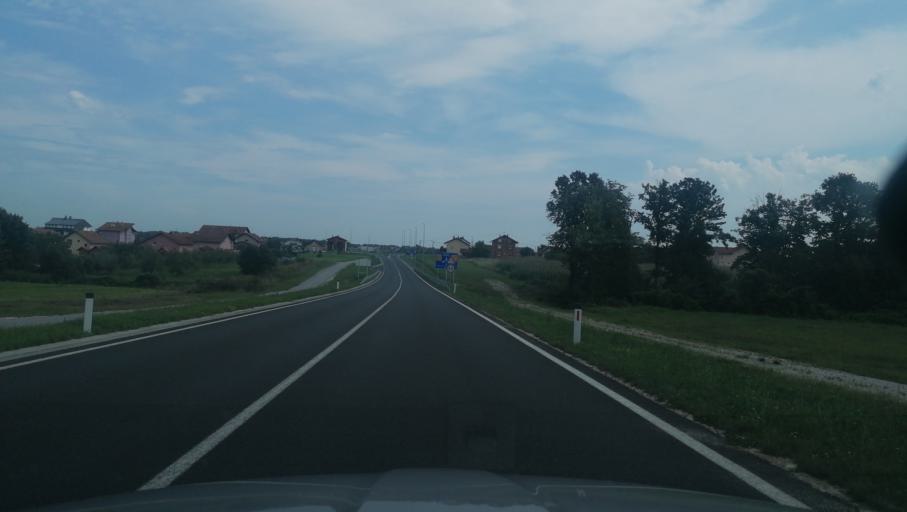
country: BA
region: Brcko
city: Brcko
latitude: 44.8283
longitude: 18.8144
